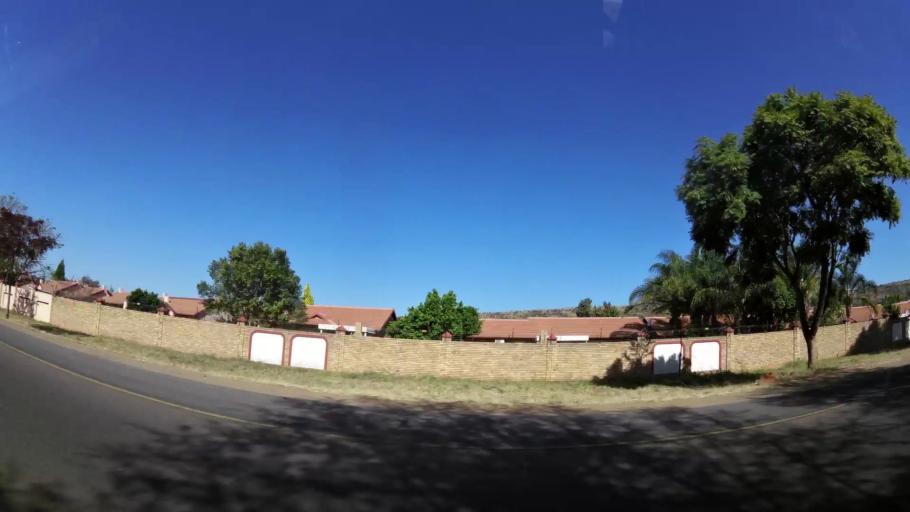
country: ZA
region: Gauteng
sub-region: City of Tshwane Metropolitan Municipality
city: Pretoria
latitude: -25.6825
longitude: 28.2303
